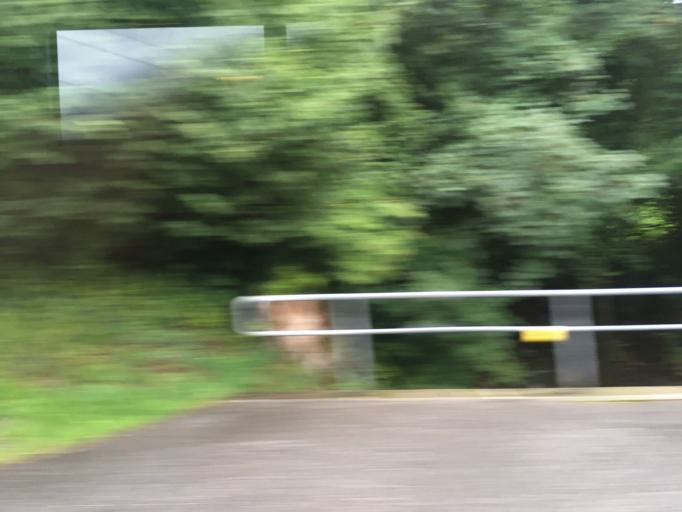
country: CH
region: Schwyz
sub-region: Bezirk Hoefe
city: Schindellegi
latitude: 47.1813
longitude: 8.7244
